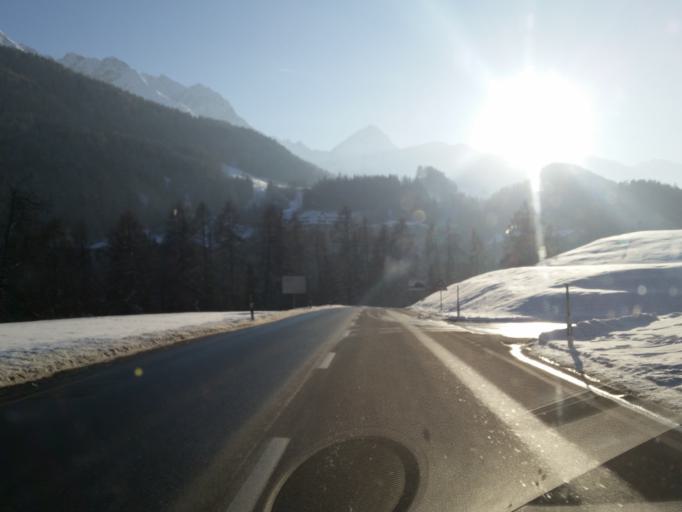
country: CH
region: Grisons
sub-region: Inn District
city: Scuol
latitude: 46.7909
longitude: 10.2873
